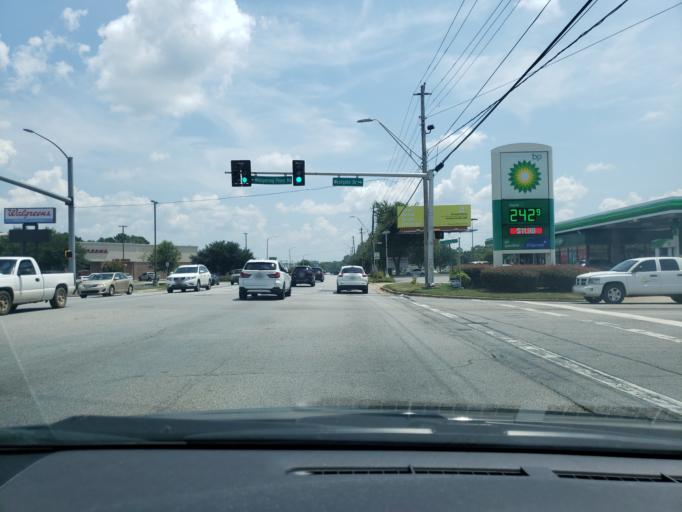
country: US
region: Georgia
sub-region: Dougherty County
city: Albany
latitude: 31.6060
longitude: -84.2071
